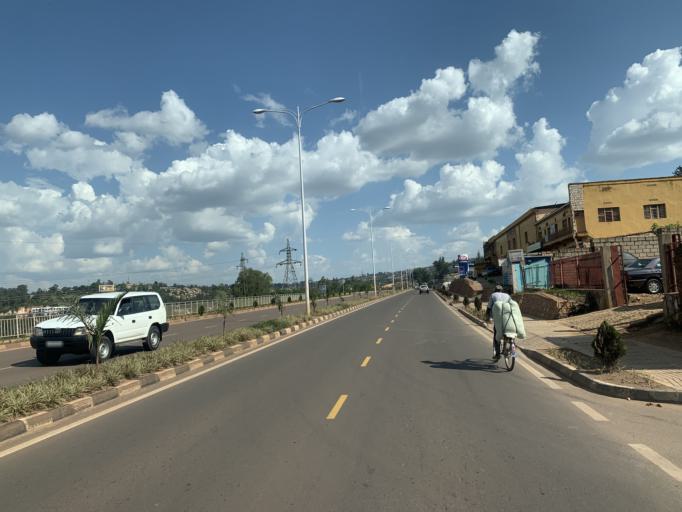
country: RW
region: Kigali
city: Kigali
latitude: -1.9666
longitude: 30.0819
